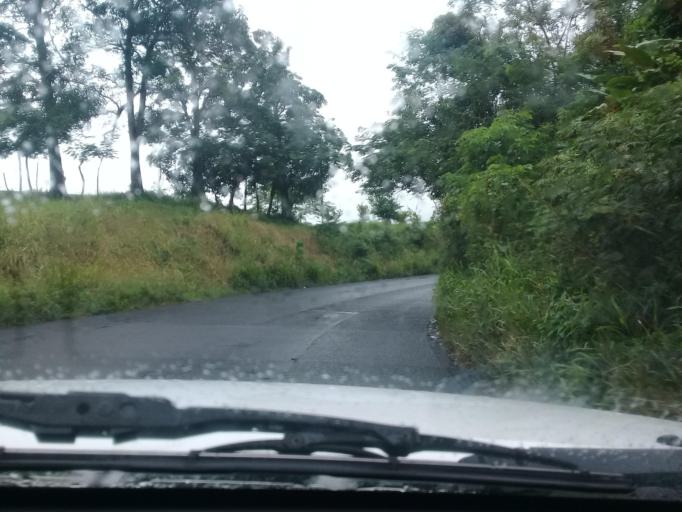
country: MX
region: Veracruz
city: Santiago Tuxtla
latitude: 18.4593
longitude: -95.2969
